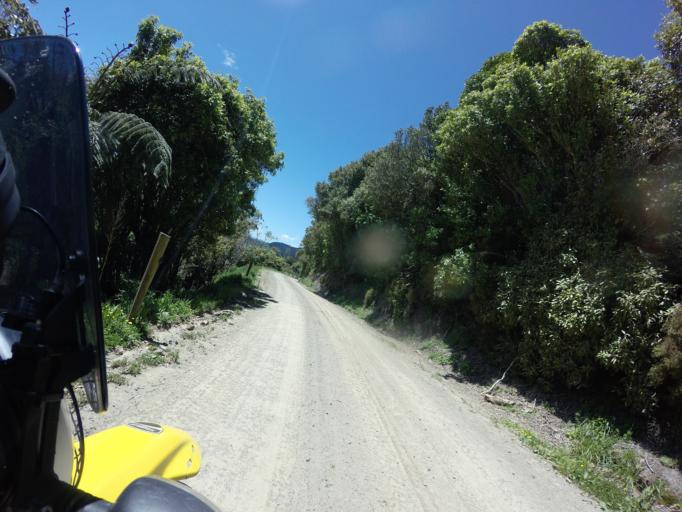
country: NZ
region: Bay of Plenty
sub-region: Opotiki District
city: Opotiki
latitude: -38.4061
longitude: 177.4477
